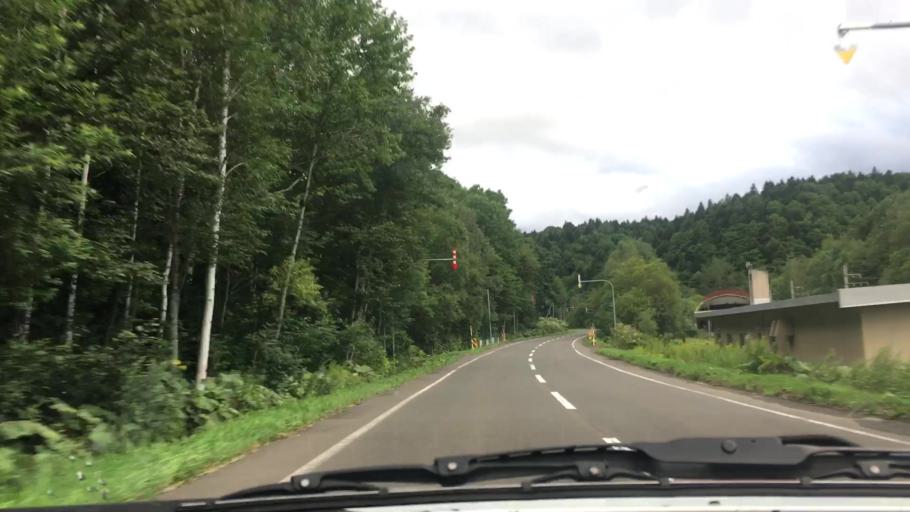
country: JP
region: Hokkaido
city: Shimo-furano
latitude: 43.0737
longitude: 142.6731
